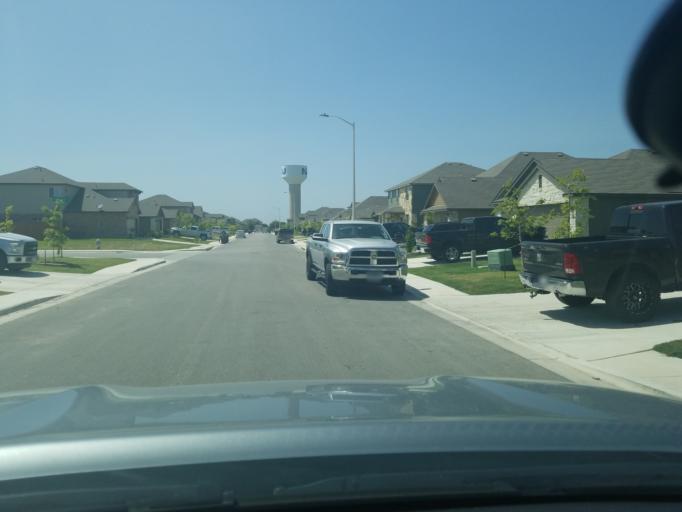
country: US
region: Texas
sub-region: Guadalupe County
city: Lake Dunlap
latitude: 29.6742
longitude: -98.0331
